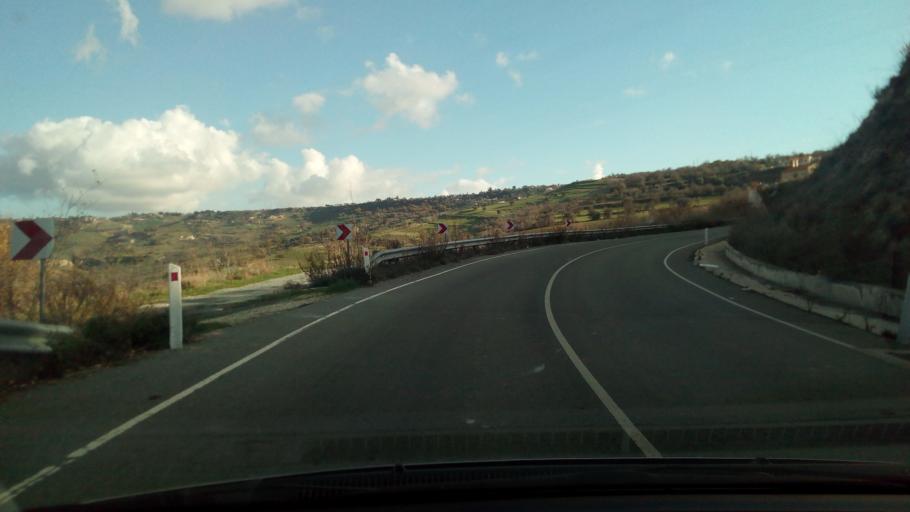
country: CY
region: Pafos
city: Tala
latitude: 34.9382
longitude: 32.5157
